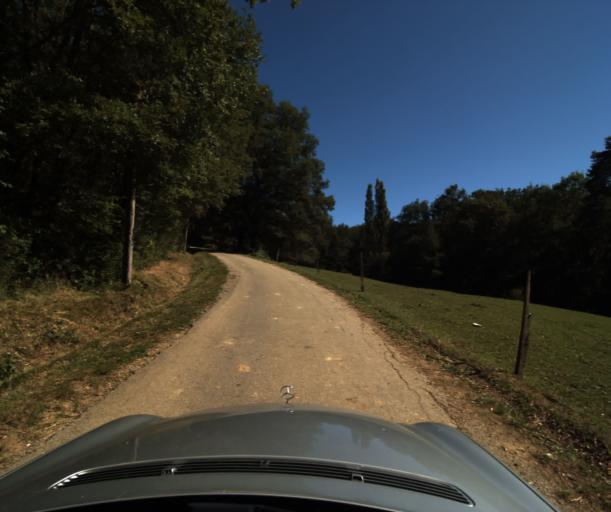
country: FR
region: Midi-Pyrenees
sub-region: Departement de l'Ariege
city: Belesta
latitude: 42.9762
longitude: 1.9108
